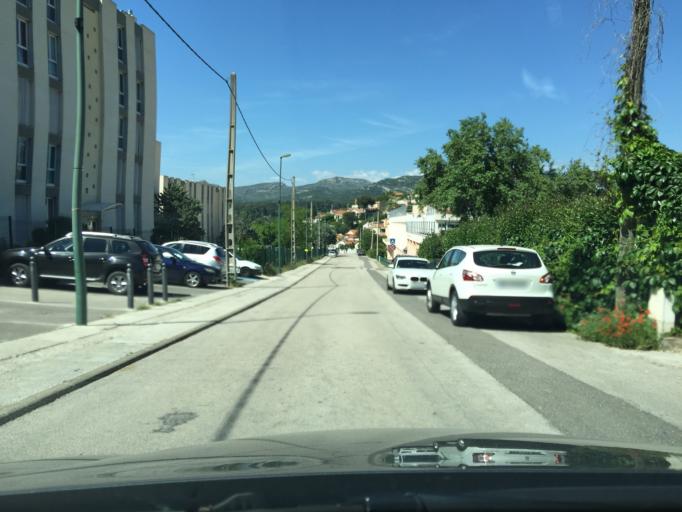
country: FR
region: Provence-Alpes-Cote d'Azur
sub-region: Departement des Bouches-du-Rhone
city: La Penne-sur-Huveaune
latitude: 43.2764
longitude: 5.5170
